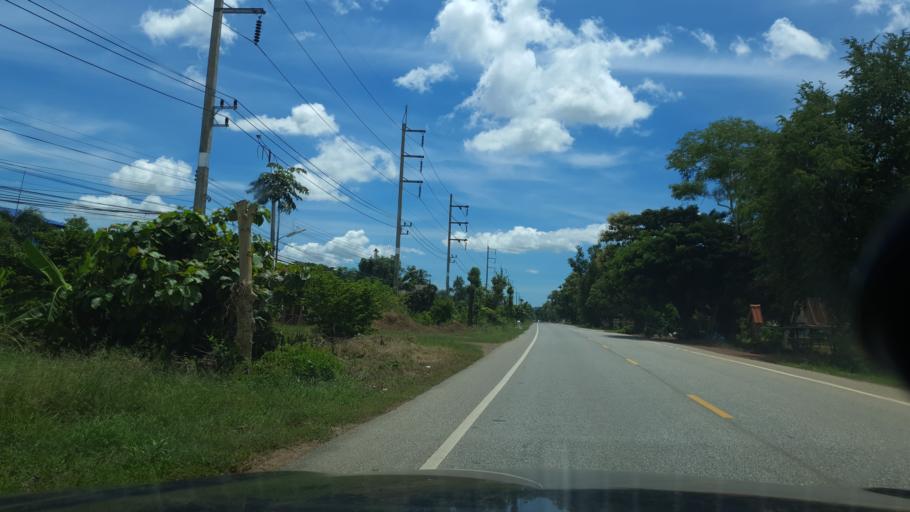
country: TH
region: Sukhothai
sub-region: Amphoe Si Satchanalai
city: Si Satchanalai
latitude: 17.4962
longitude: 99.7589
